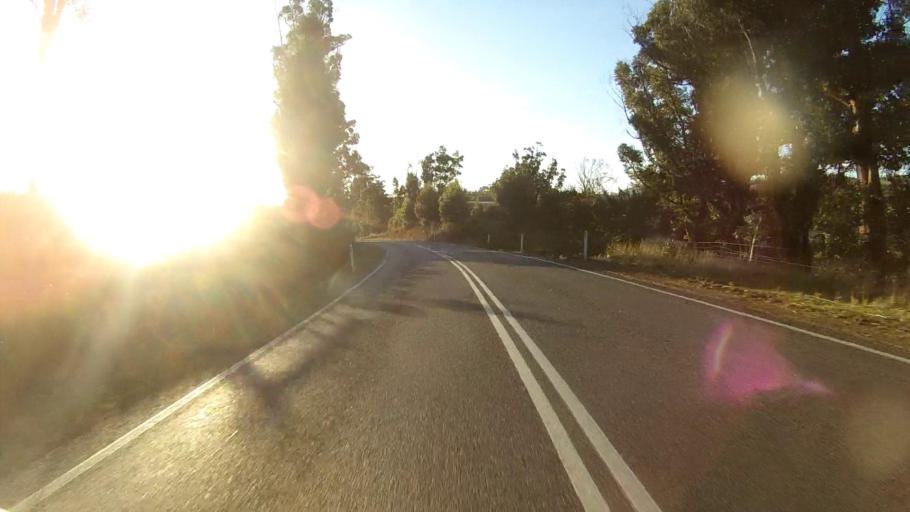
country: AU
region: Tasmania
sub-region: Sorell
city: Sorell
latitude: -42.8425
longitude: 147.8114
